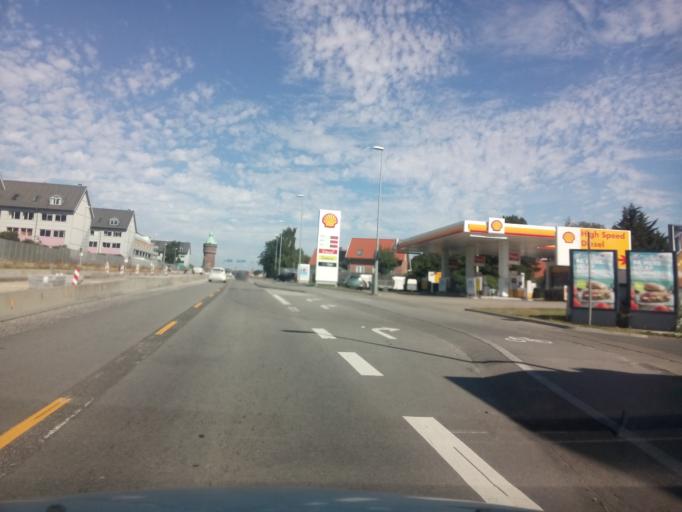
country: DK
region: Central Jutland
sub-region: Arhus Kommune
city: Arhus
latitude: 56.1798
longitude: 10.1994
